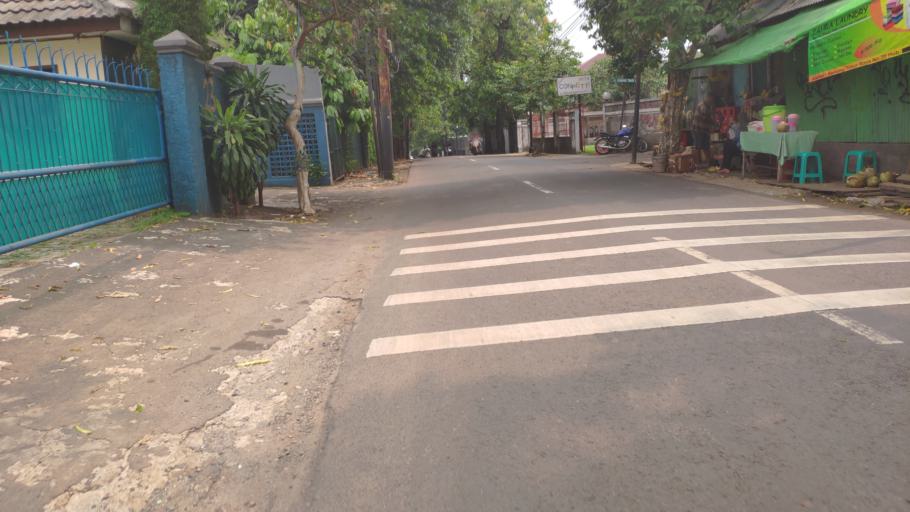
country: ID
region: Jakarta Raya
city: Jakarta
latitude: -6.2609
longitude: 106.8234
